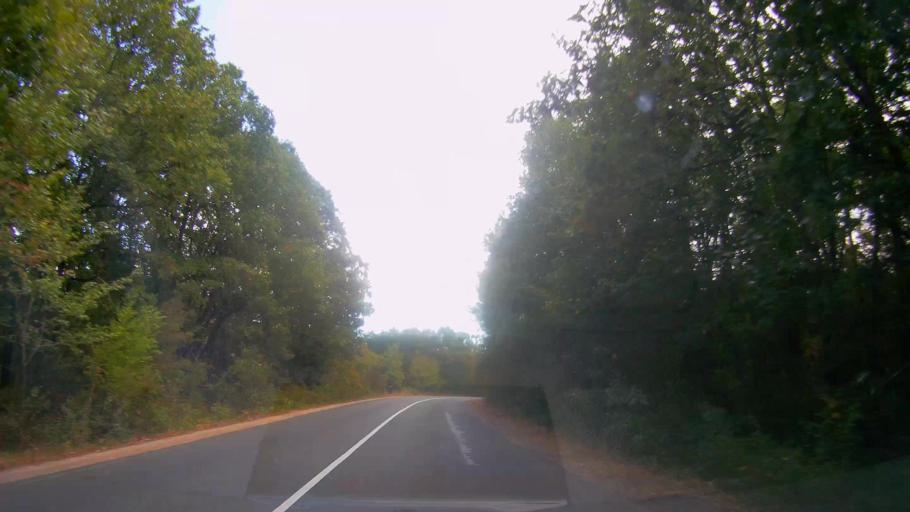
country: BG
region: Burgas
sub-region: Obshtina Primorsko
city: Primorsko
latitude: 42.2920
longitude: 27.7331
